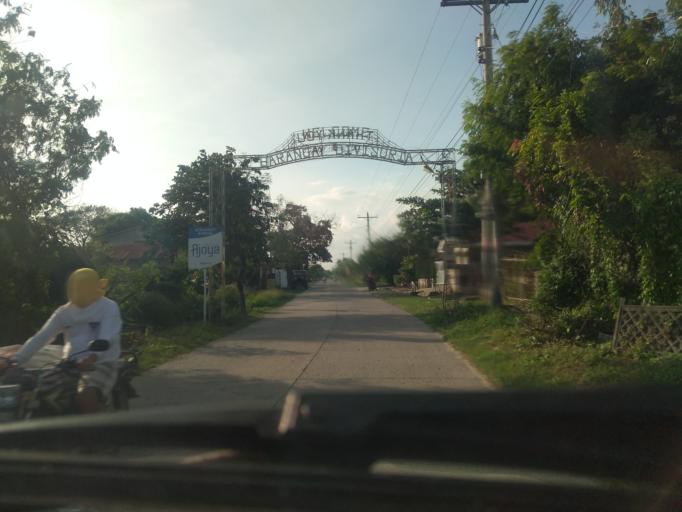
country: PH
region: Central Luzon
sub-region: Province of Pampanga
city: Bulaon
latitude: 15.0876
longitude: 120.6933
